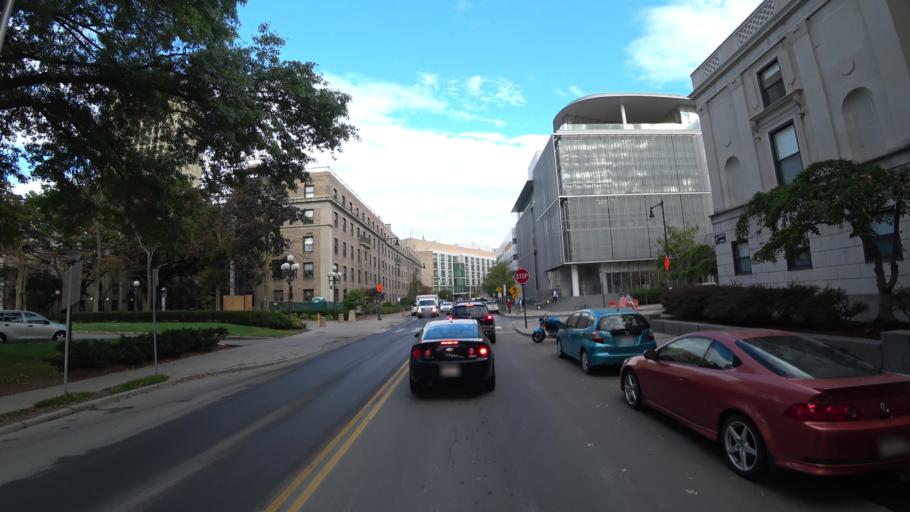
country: US
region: Massachusetts
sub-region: Middlesex County
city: Cambridge
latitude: 42.3598
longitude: -71.0874
